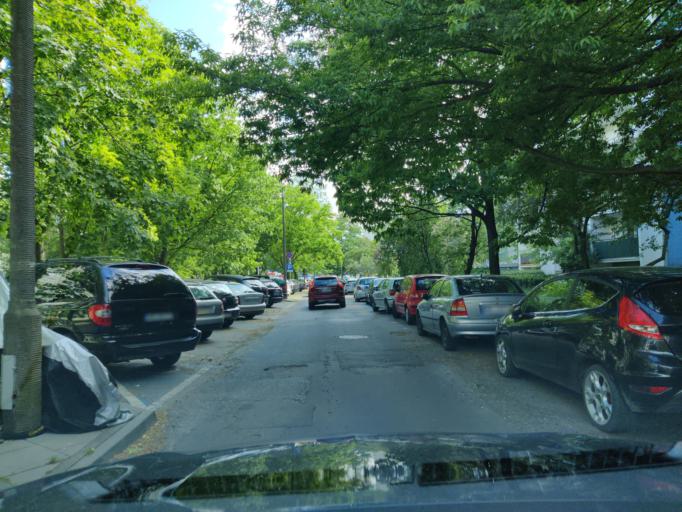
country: PL
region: Masovian Voivodeship
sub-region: Warszawa
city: Mokotow
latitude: 52.1810
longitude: 21.0119
